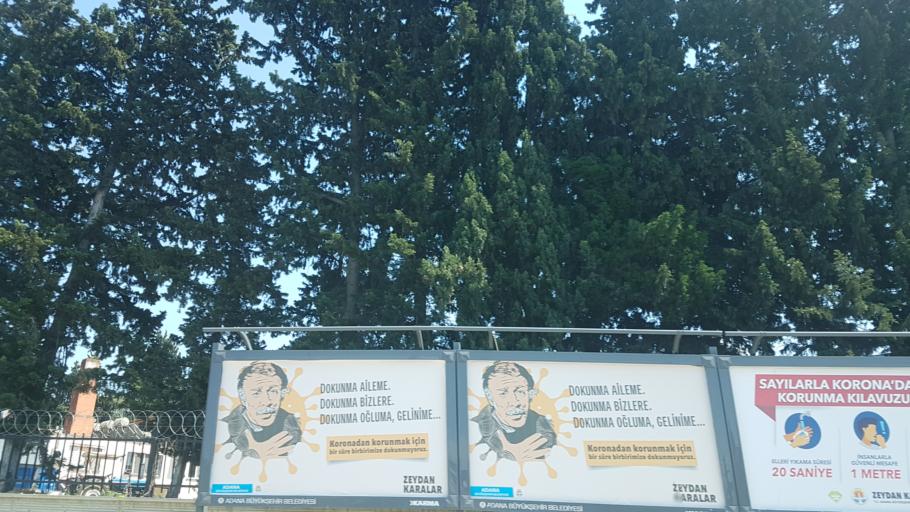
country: TR
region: Adana
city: Adana
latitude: 37.0135
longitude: 35.3379
